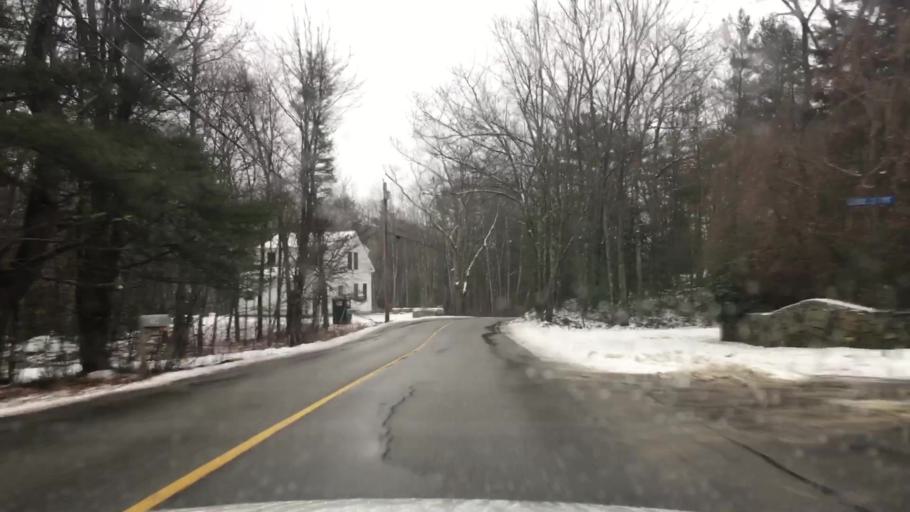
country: US
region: Maine
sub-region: York County
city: Kennebunkport
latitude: 43.3730
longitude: -70.4544
